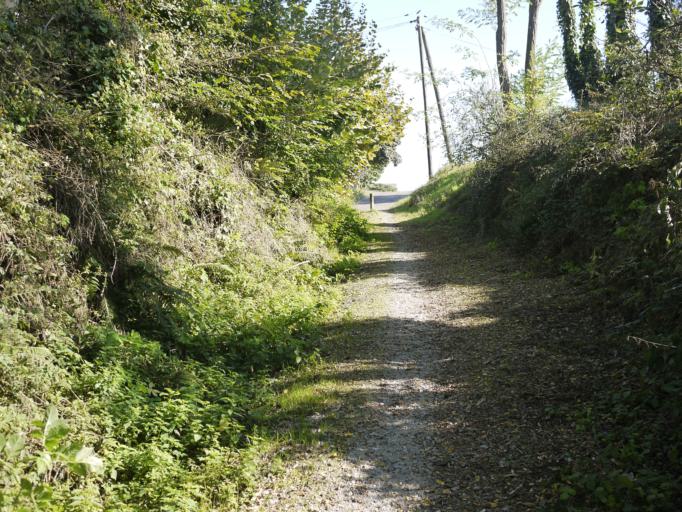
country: FR
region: Aquitaine
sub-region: Departement des Landes
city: Saint-Paul-les-Dax
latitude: 43.7240
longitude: -1.0654
